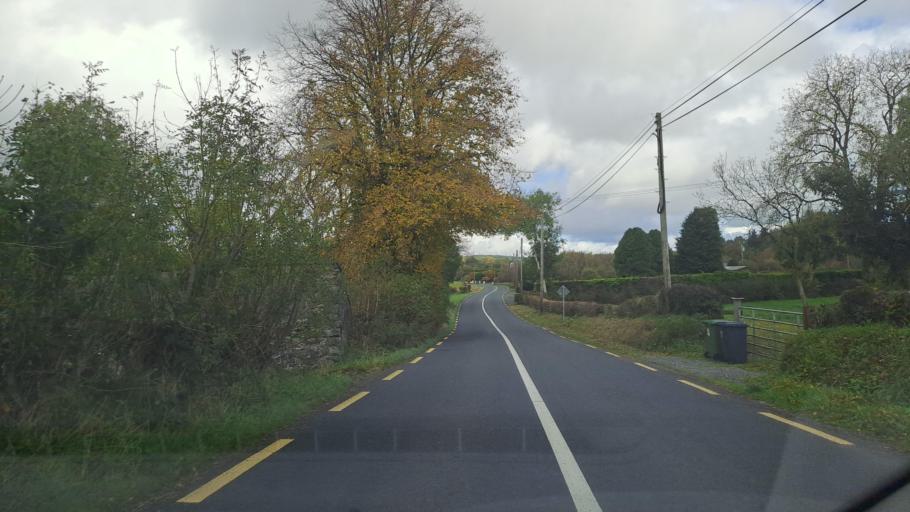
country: IE
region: Ulster
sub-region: An Cabhan
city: Bailieborough
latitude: 53.8861
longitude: -6.9640
